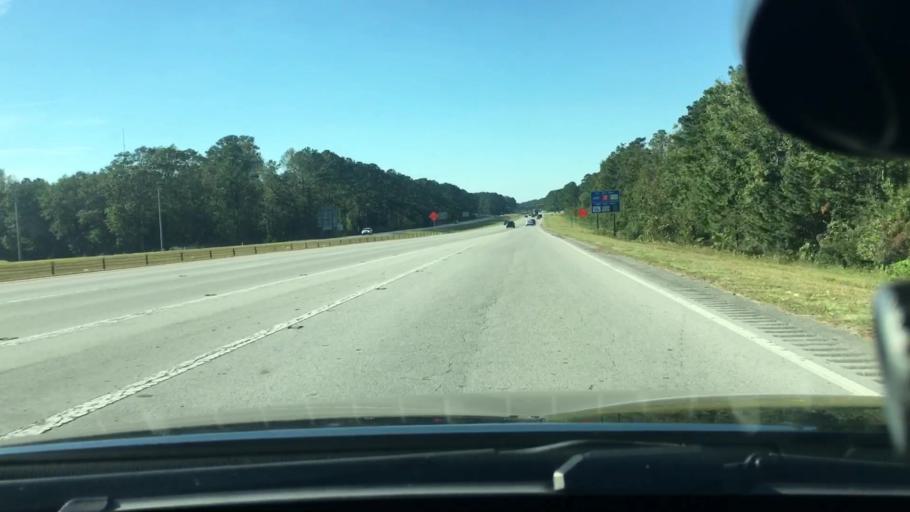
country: US
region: North Carolina
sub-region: Craven County
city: Trent Woods
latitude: 35.1059
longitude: -77.0868
